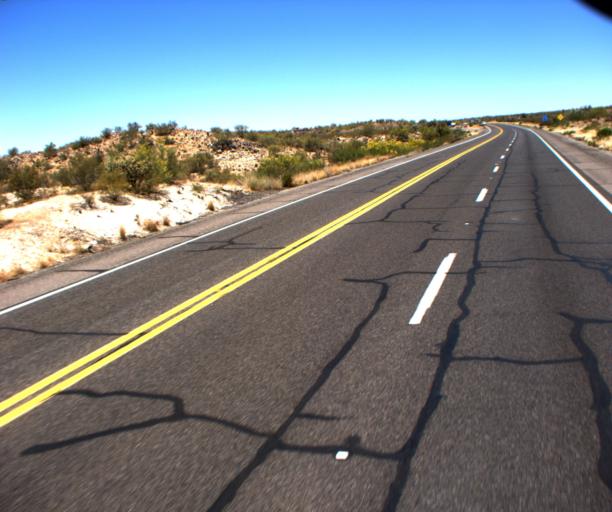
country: US
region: Arizona
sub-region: Yavapai County
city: Congress
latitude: 34.2244
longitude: -113.0694
